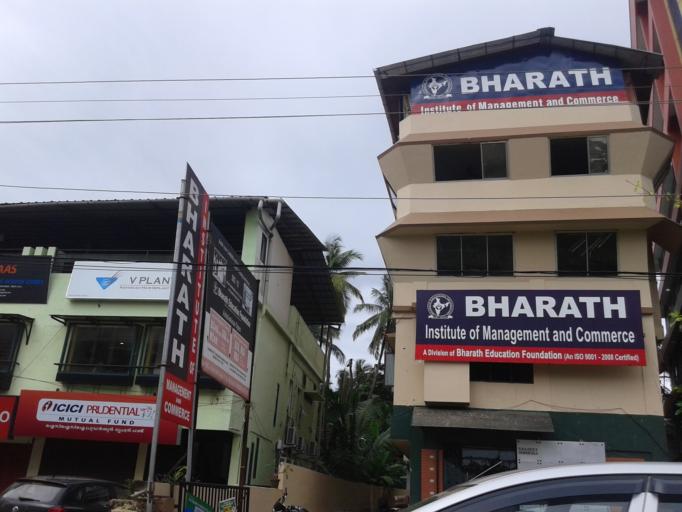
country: IN
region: Kerala
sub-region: Kozhikode
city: Kozhikode
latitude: 11.2589
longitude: 75.7776
